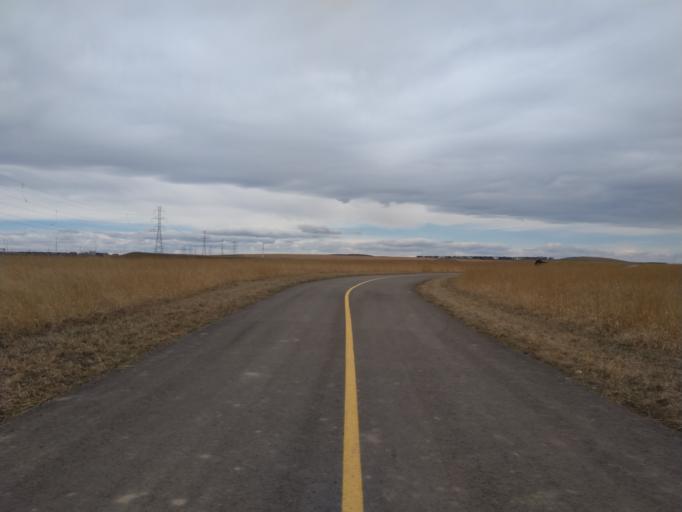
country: CA
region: Alberta
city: Airdrie
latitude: 51.1774
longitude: -114.0293
